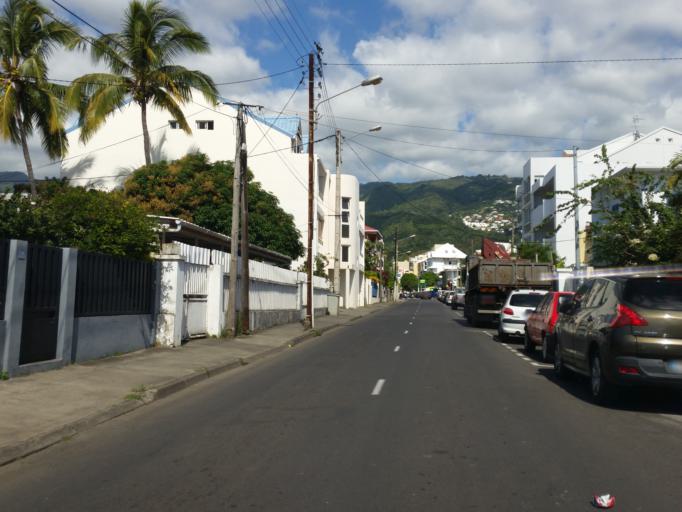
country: RE
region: Reunion
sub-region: Reunion
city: Saint-Denis
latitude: -20.8856
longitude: 55.4592
